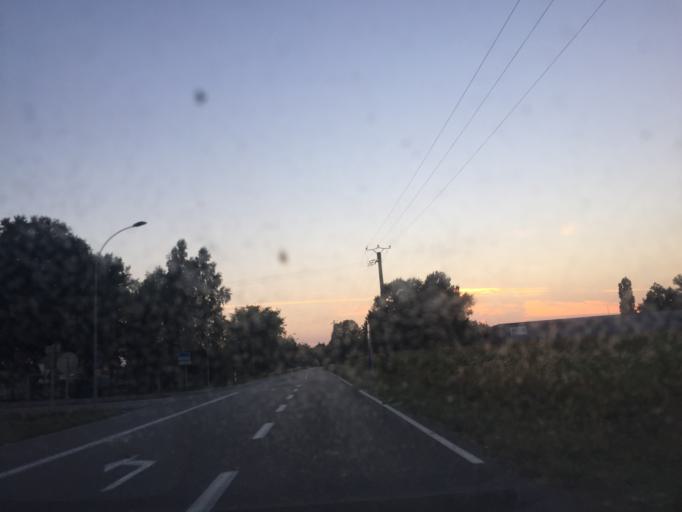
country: FR
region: Rhone-Alpes
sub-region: Departement de l'Ain
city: Mionnay
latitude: 45.8712
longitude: 4.9237
